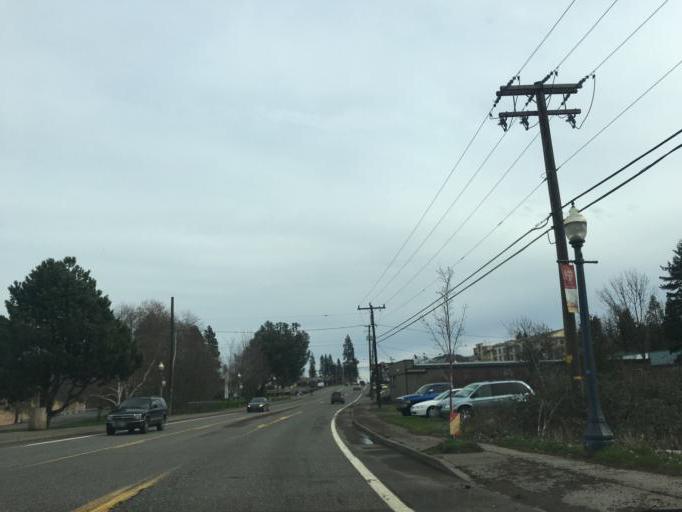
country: US
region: Oregon
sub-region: Hood River County
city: Hood River
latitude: 45.7109
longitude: -121.5410
